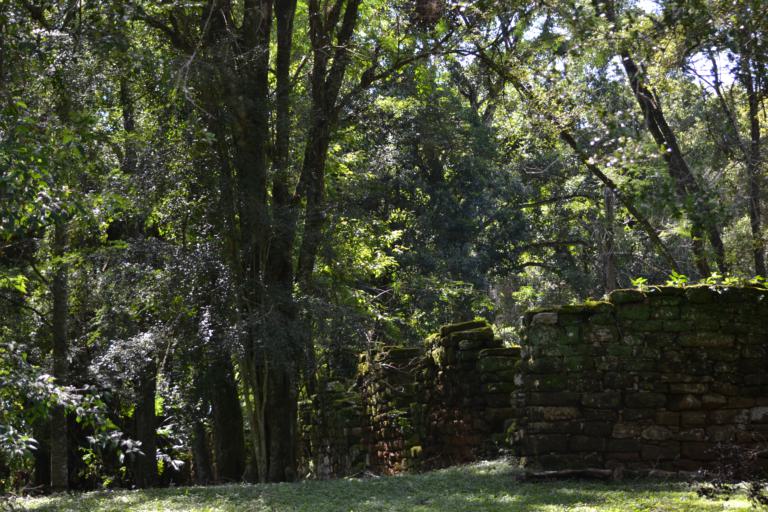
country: AR
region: Misiones
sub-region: Departamento de San Ignacio
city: San Ignacio
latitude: -27.2548
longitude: -55.5299
